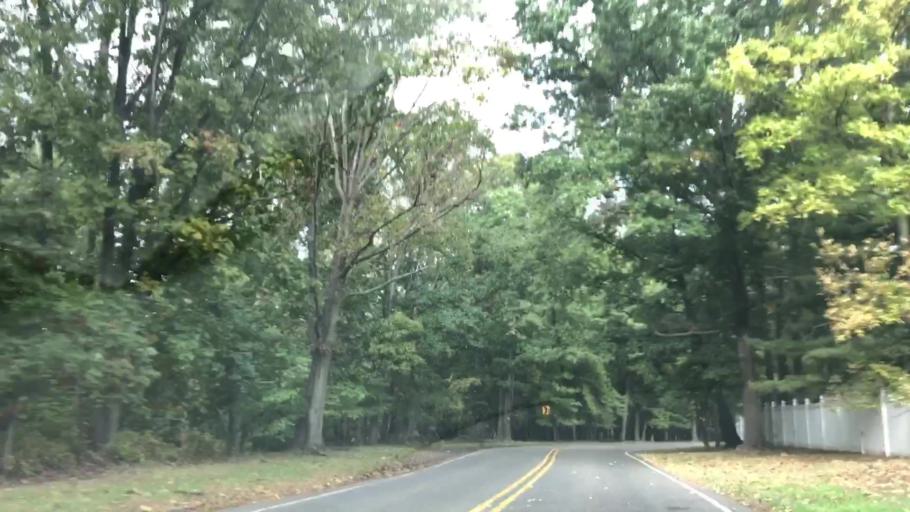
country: US
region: New Jersey
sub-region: Union County
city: Winfield
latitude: 40.6330
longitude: -74.2849
